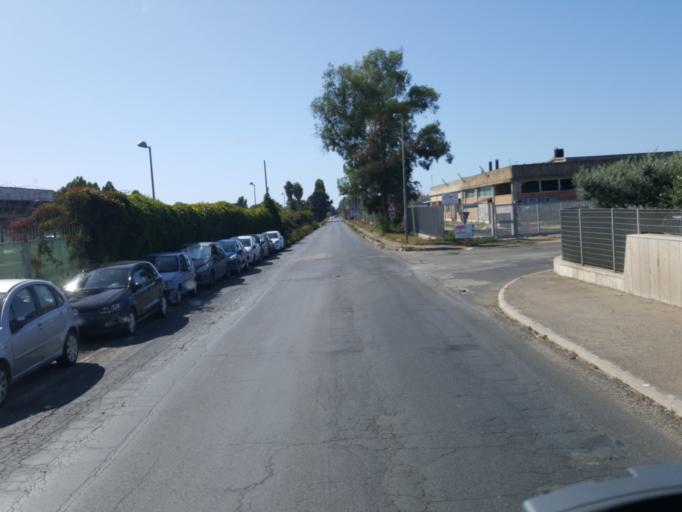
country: IT
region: Latium
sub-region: Citta metropolitana di Roma Capitale
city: Anzio
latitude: 41.5136
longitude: 12.6261
